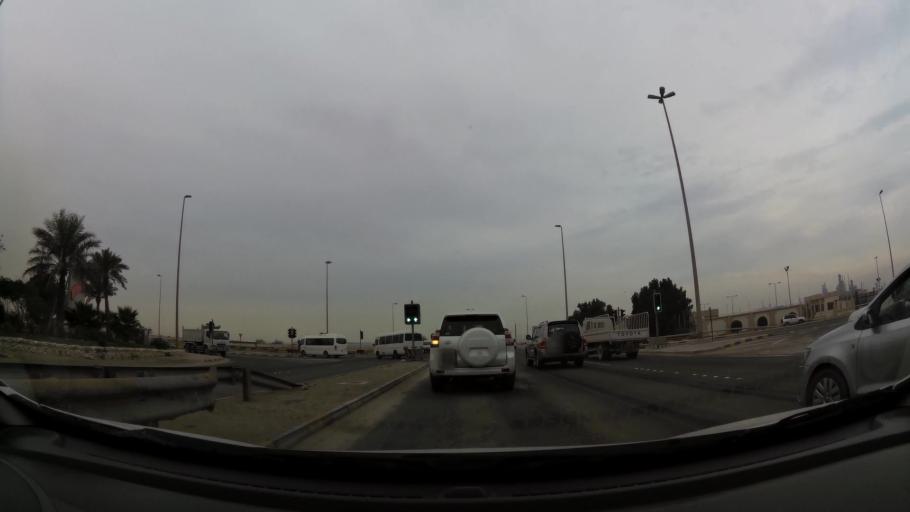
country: BH
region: Northern
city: Sitrah
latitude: 26.0980
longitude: 50.6064
